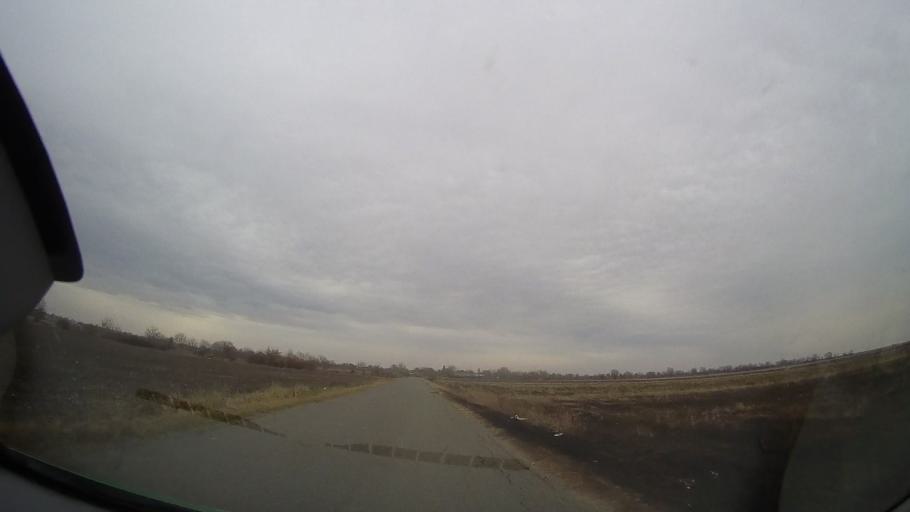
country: RO
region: Prahova
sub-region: Comuna Fantanele
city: Fantanele
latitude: 45.0076
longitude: 26.3596
